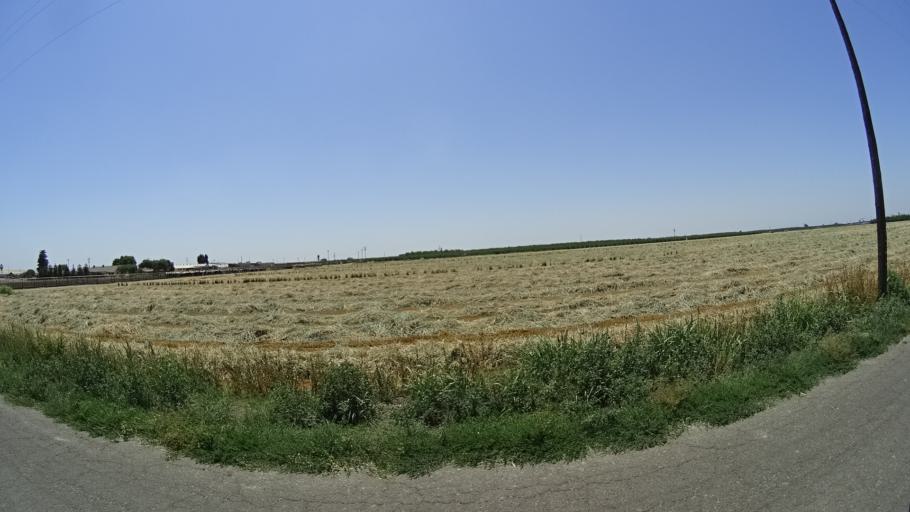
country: US
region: California
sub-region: Fresno County
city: Laton
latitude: 36.3863
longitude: -119.7294
